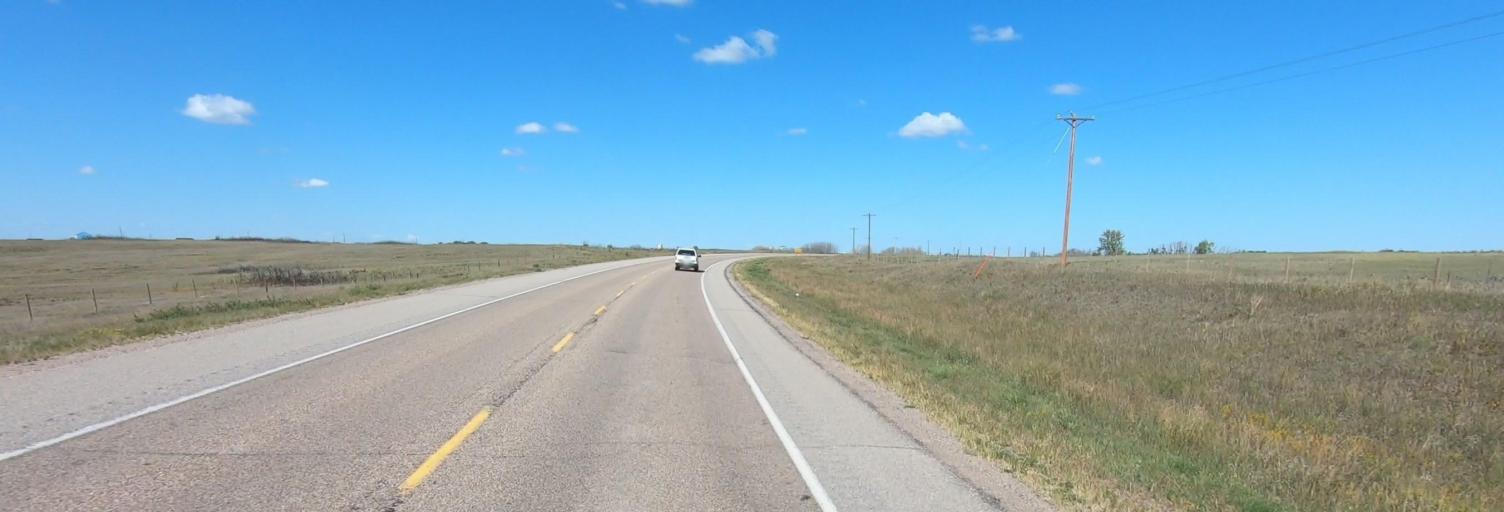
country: CA
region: Alberta
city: Strathmore
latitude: 50.8725
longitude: -113.1610
